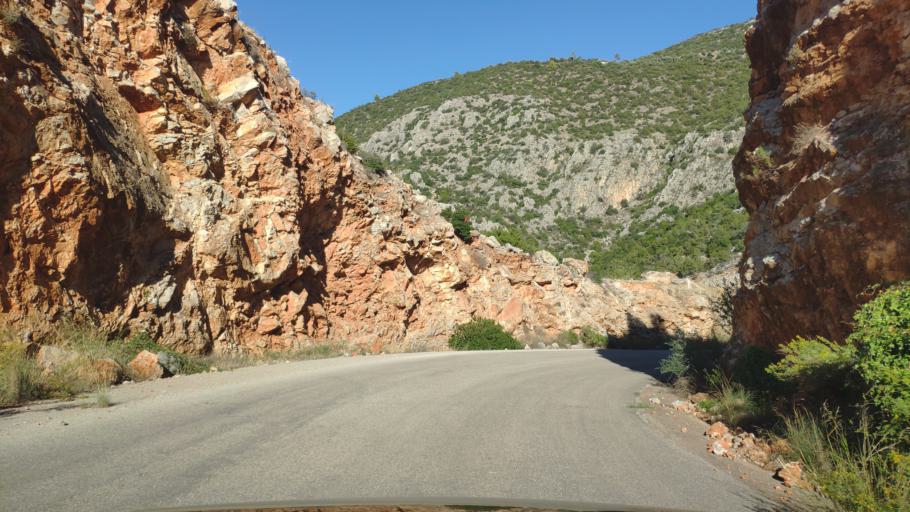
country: GR
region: Attica
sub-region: Nomos Piraios
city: Galatas
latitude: 37.5684
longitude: 23.3594
